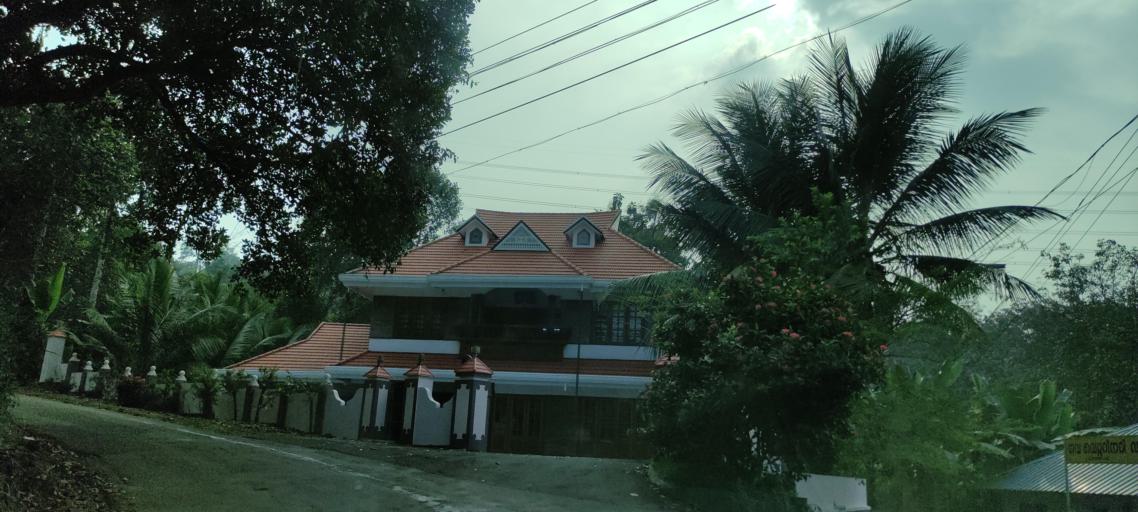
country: IN
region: Kerala
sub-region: Ernakulam
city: Piravam
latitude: 9.8103
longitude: 76.5343
